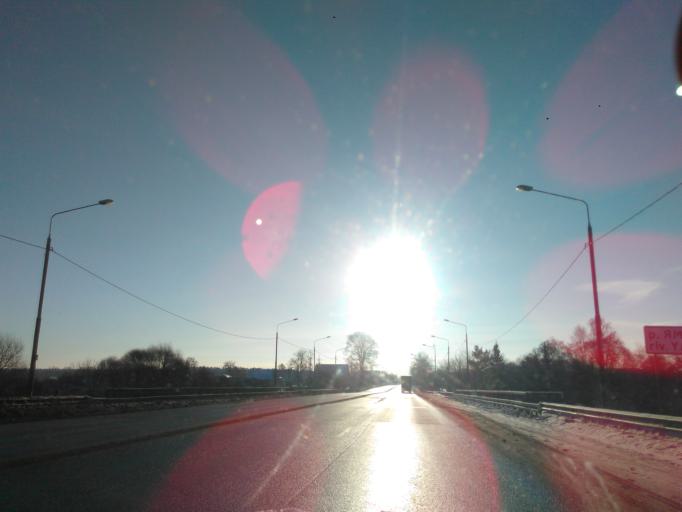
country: RU
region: Moskovskaya
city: Klin
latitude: 56.3885
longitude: 36.6653
